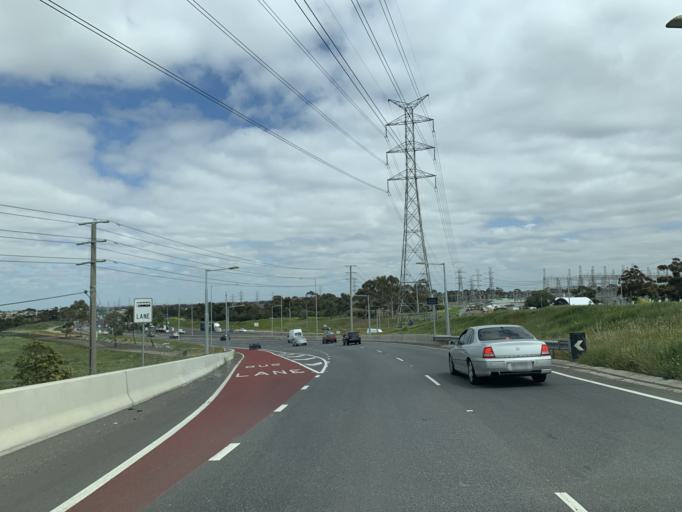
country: AU
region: Victoria
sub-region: Moonee Valley
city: Keilor East
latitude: -37.7399
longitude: 144.8515
